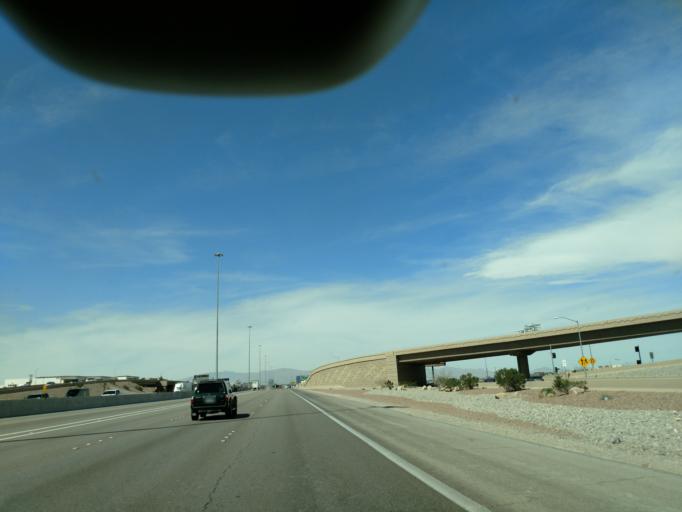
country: US
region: Nevada
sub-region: Clark County
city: Paradise
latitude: 36.0442
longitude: -115.1806
